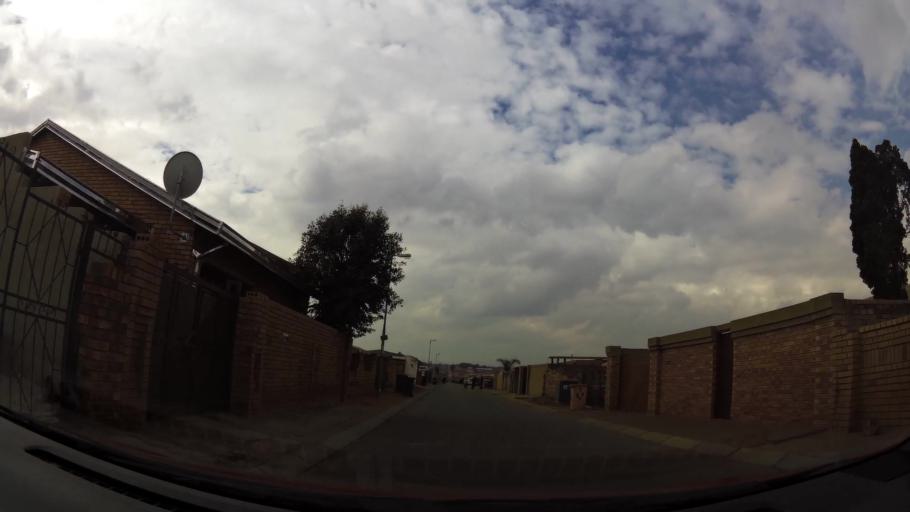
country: ZA
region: Gauteng
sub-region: City of Johannesburg Metropolitan Municipality
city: Soweto
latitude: -26.2496
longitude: 27.8332
